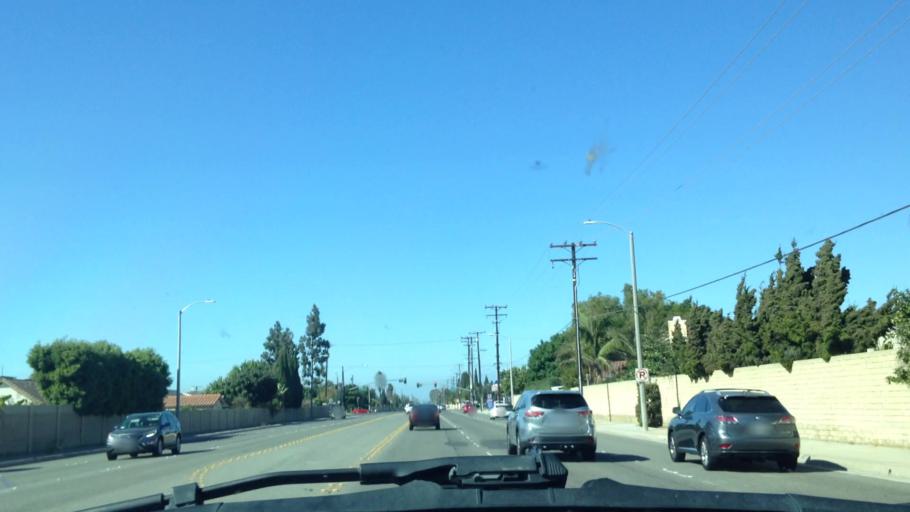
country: US
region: California
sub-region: Orange County
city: Midway City
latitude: 33.7283
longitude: -117.9720
